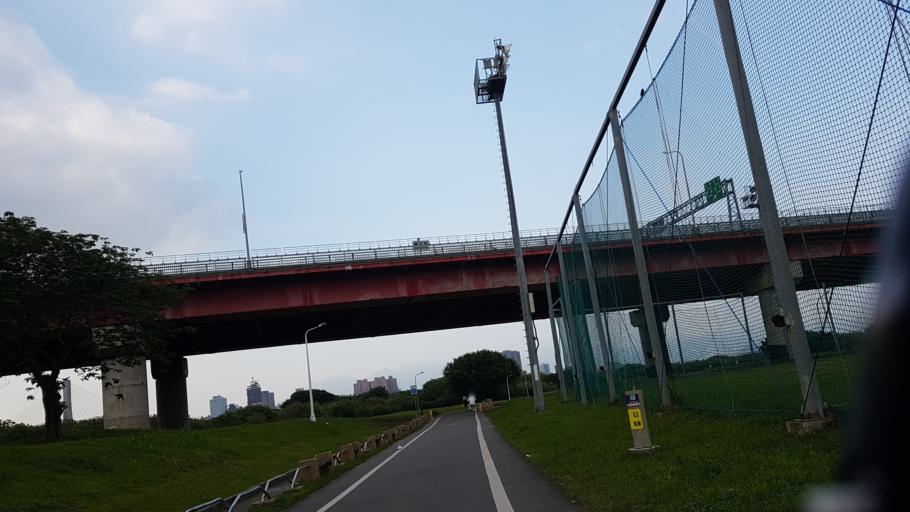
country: TW
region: Taipei
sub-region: Taipei
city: Banqiao
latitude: 25.0350
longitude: 121.4866
